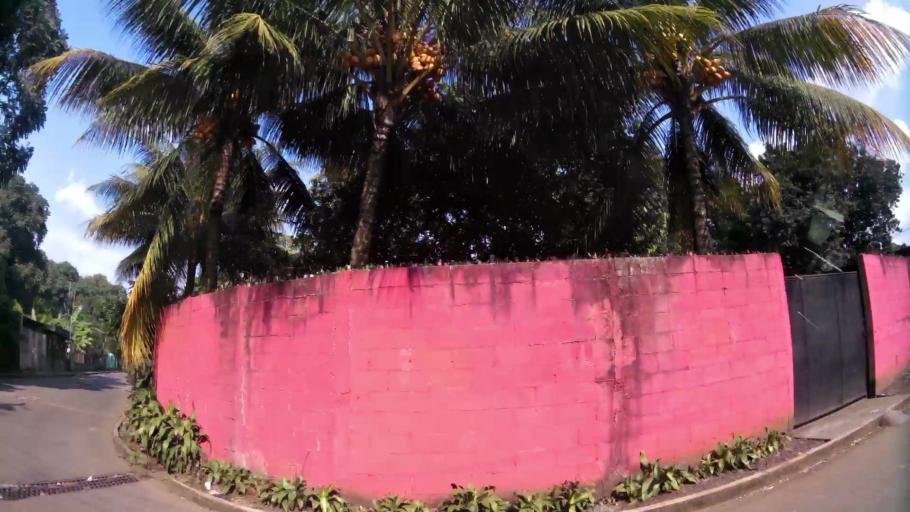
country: GT
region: Retalhuleu
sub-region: Municipio de Retalhuleu
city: Retalhuleu
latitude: 14.5352
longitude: -91.6934
